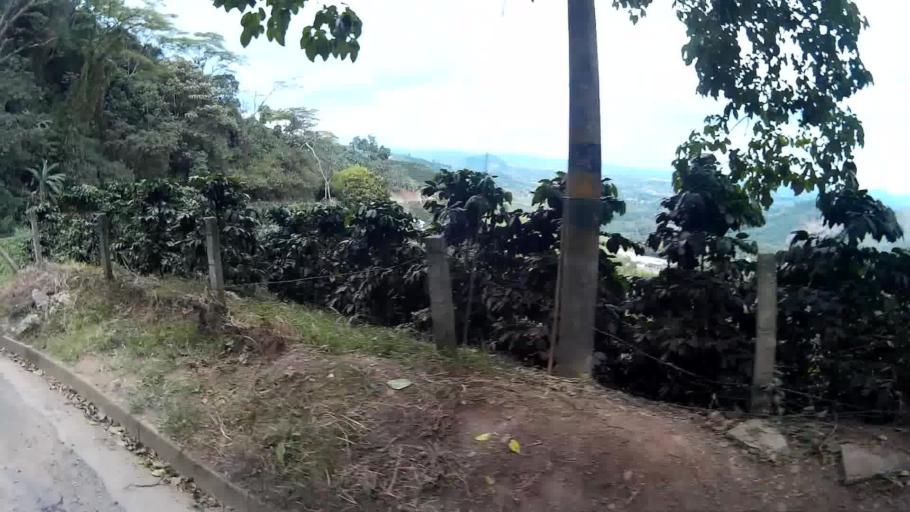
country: CO
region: Risaralda
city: Marsella
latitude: 4.8723
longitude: -75.7625
